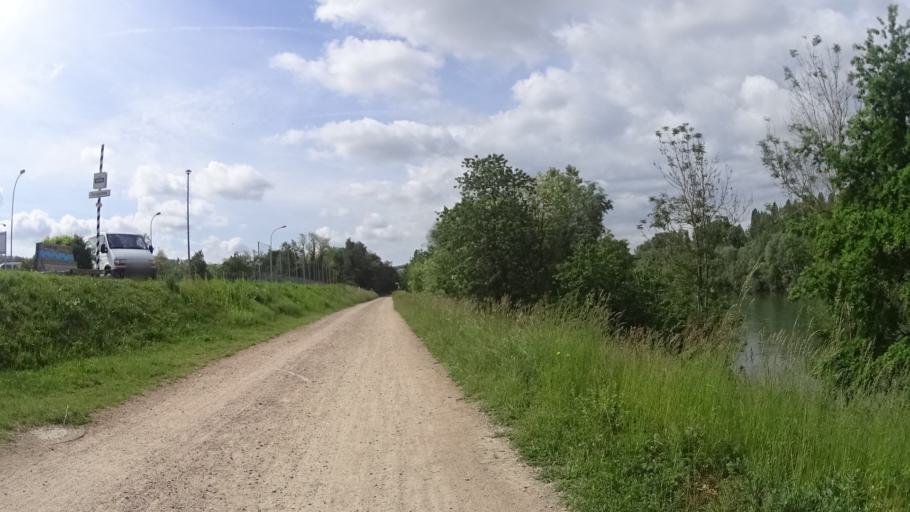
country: DE
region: Baden-Wuerttemberg
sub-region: Freiburg Region
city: Bad Bellingen
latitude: 47.7355
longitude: 7.5500
